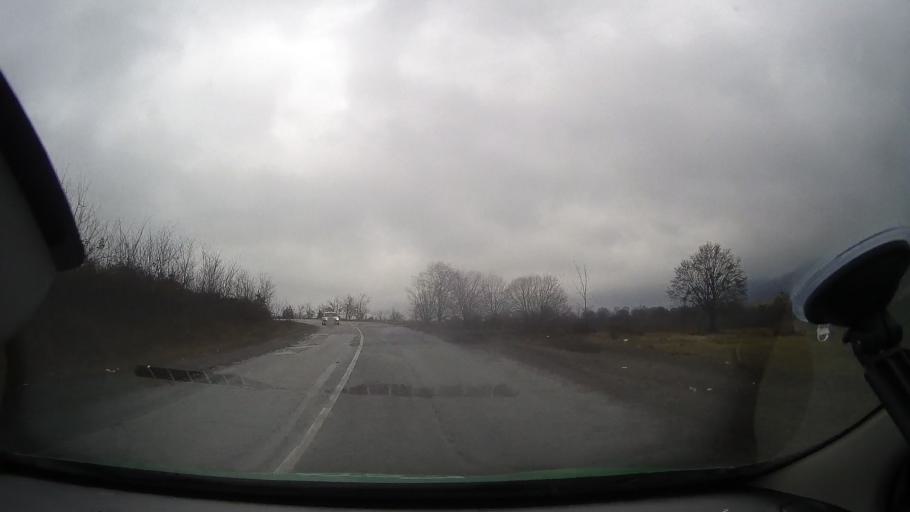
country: RO
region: Arad
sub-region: Comuna Varfurile
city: Varfurile
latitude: 46.2996
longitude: 22.5351
